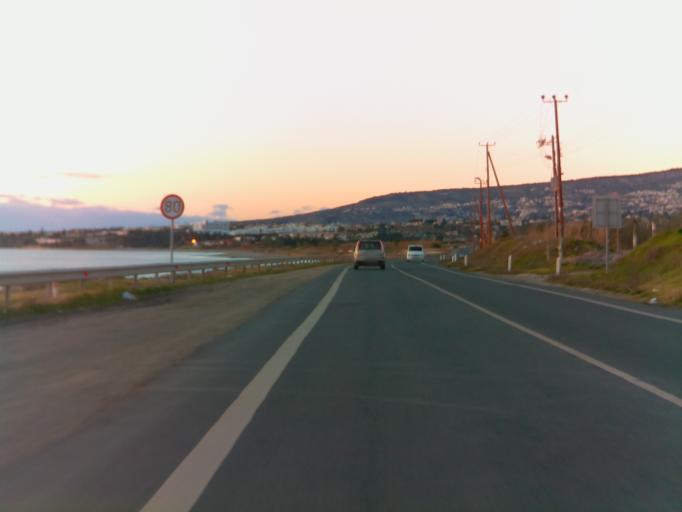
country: CY
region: Pafos
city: Kissonerga
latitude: 34.8363
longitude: 32.3904
